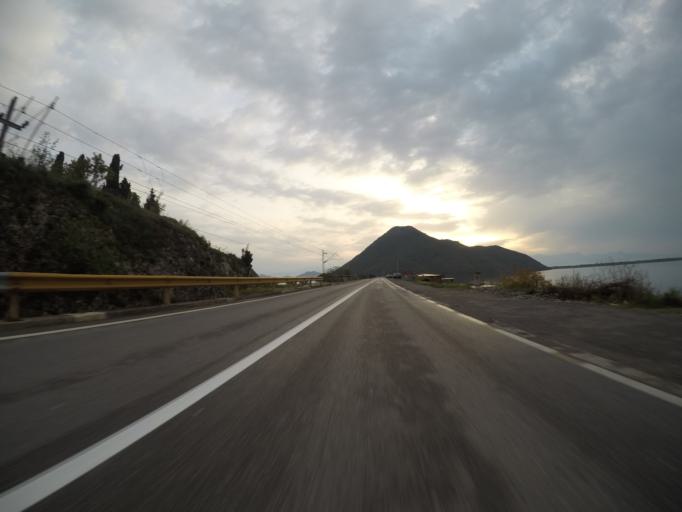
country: ME
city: Mojanovici
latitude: 42.2671
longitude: 19.1117
